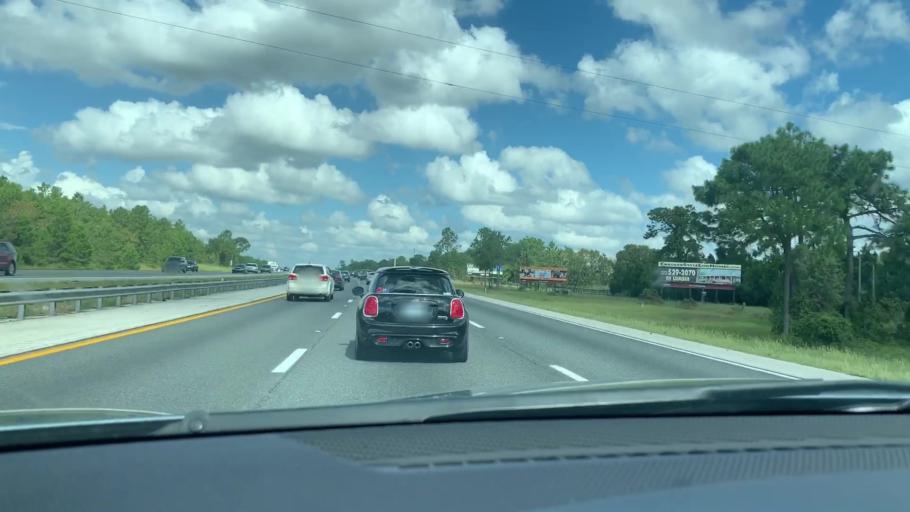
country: US
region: Florida
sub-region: Marion County
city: Belleview
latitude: 29.0565
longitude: -82.1713
